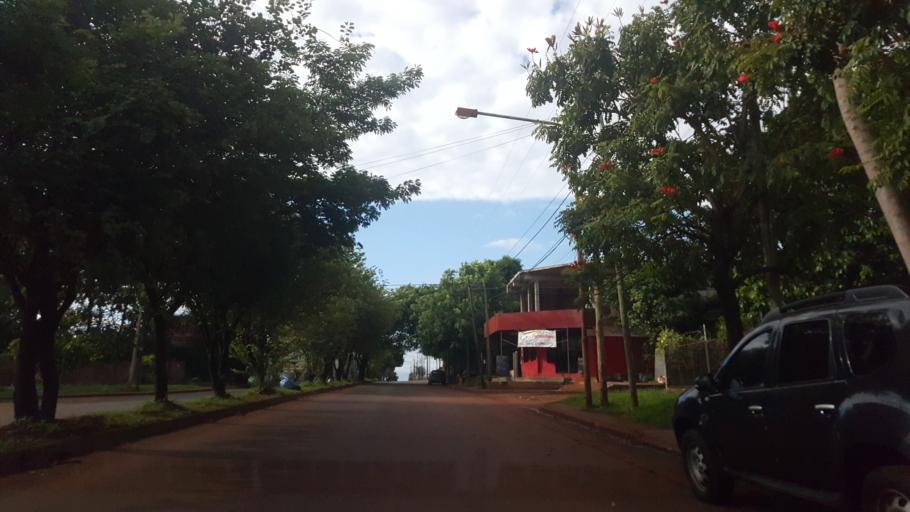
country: AR
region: Misiones
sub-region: Departamento de Capital
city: Posadas
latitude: -27.3885
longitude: -55.9346
